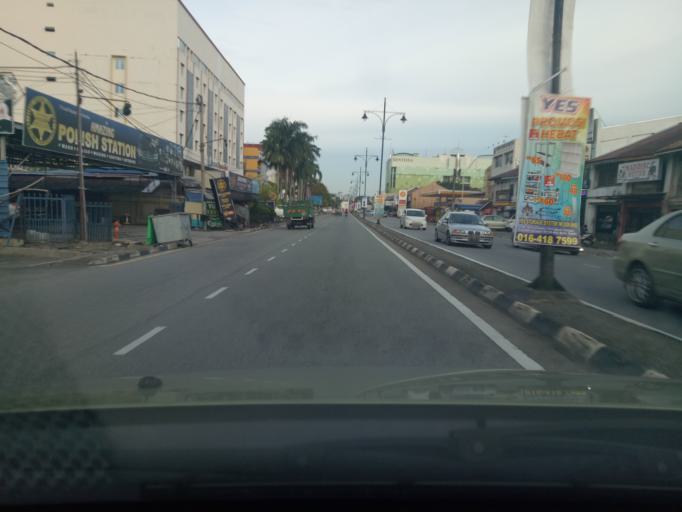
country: MY
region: Kedah
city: Alor Setar
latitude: 6.1238
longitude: 100.3609
